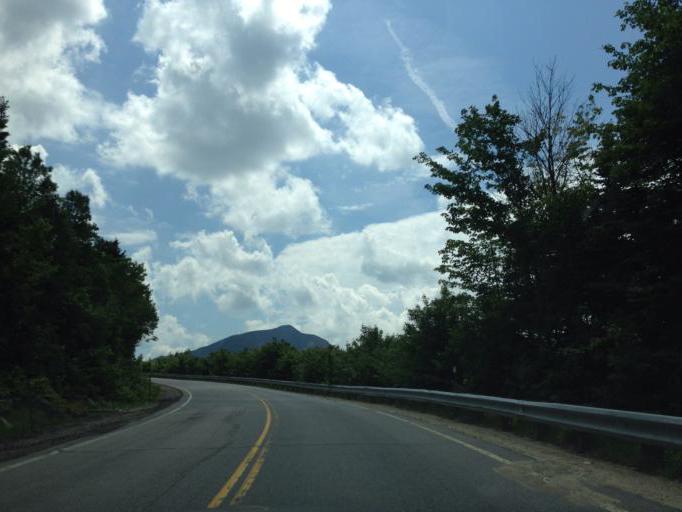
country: US
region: New Hampshire
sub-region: Grafton County
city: Woodstock
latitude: 44.0327
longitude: -71.4986
